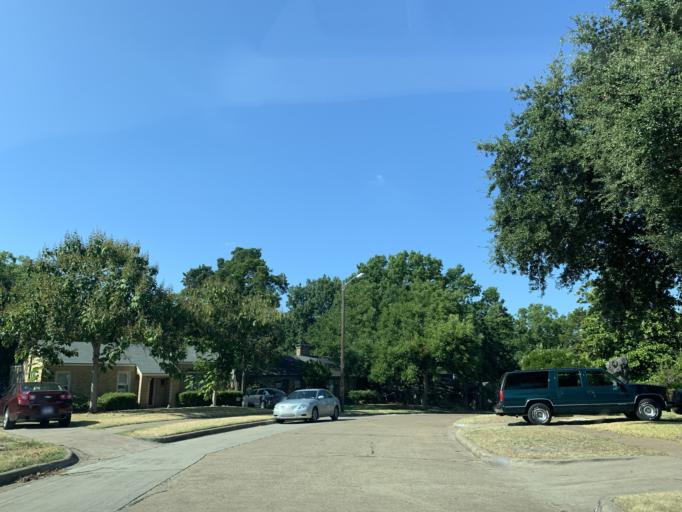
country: US
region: Texas
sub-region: Dallas County
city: Cockrell Hill
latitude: 32.7443
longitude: -96.8663
